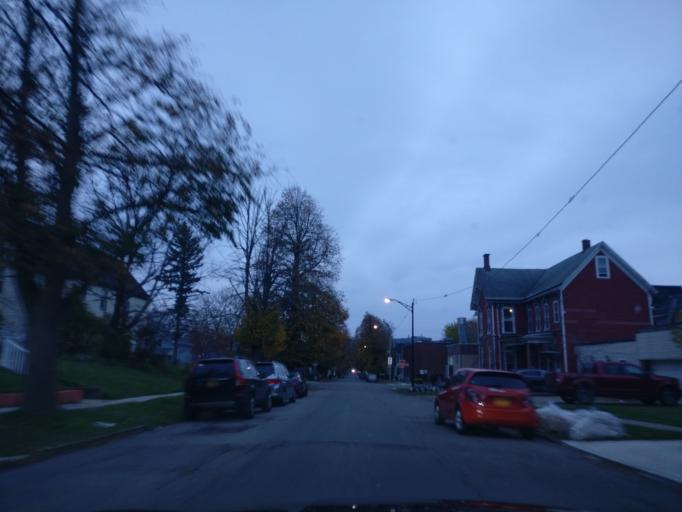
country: US
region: New York
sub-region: Erie County
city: Buffalo
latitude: 42.8989
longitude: -78.8847
